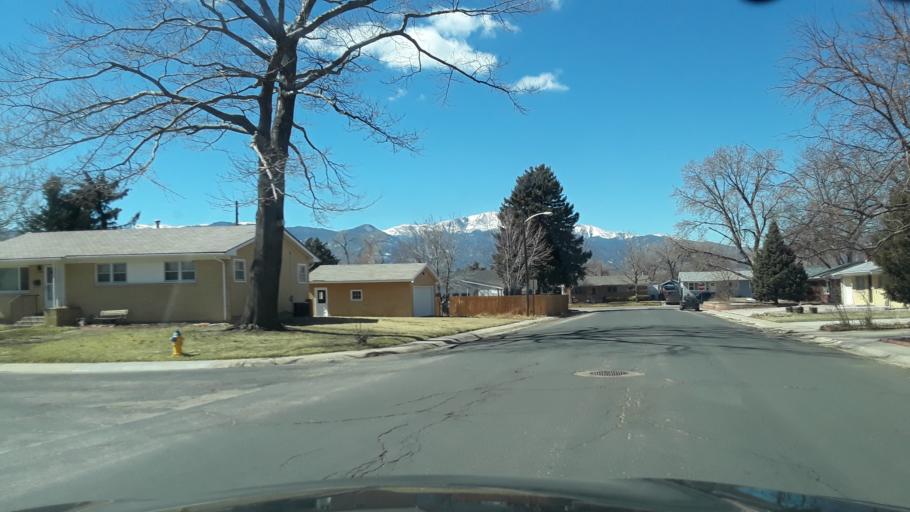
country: US
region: Colorado
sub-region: El Paso County
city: Colorado Springs
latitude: 38.8783
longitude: -104.7996
